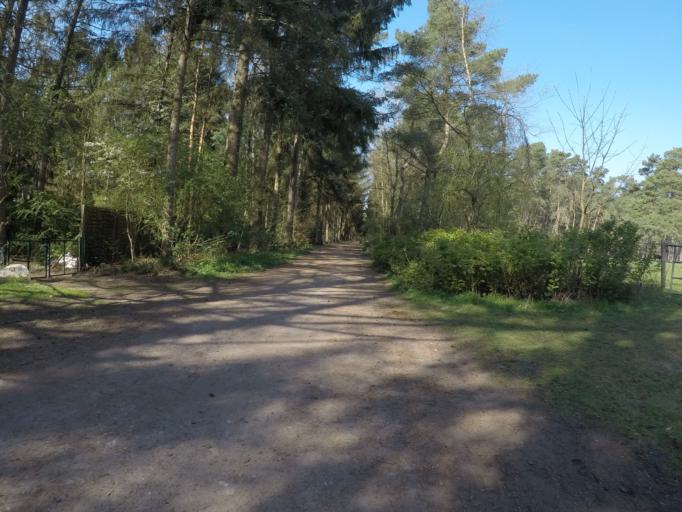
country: DE
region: Schleswig-Holstein
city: Pinneberg
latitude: 53.6193
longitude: 9.7747
